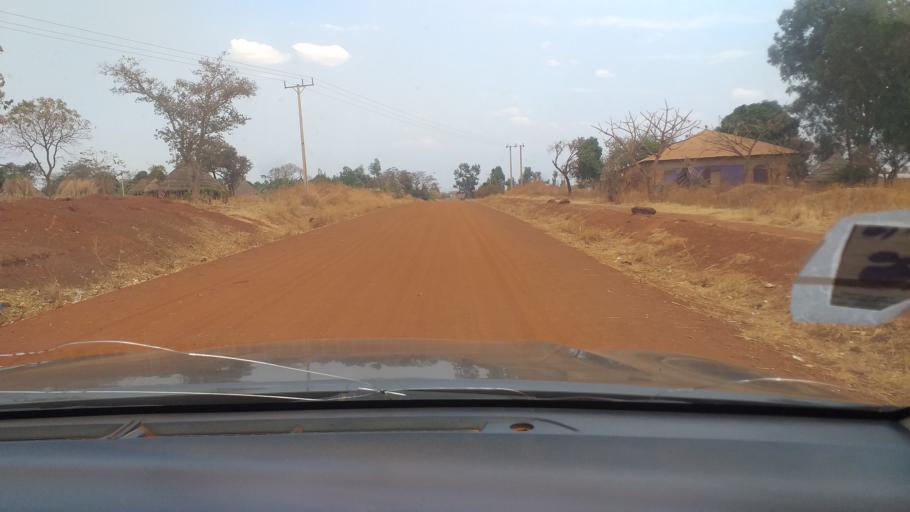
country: ET
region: Binshangul Gumuz
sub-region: Asosa
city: Asosa
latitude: 10.0624
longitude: 34.6927
